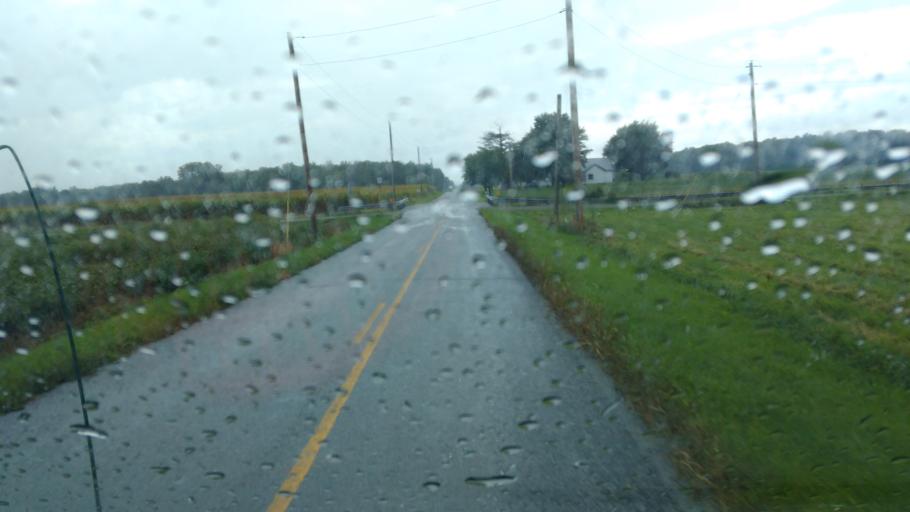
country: US
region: Ohio
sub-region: Hardin County
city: Kenton
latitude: 40.7175
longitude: -83.5943
